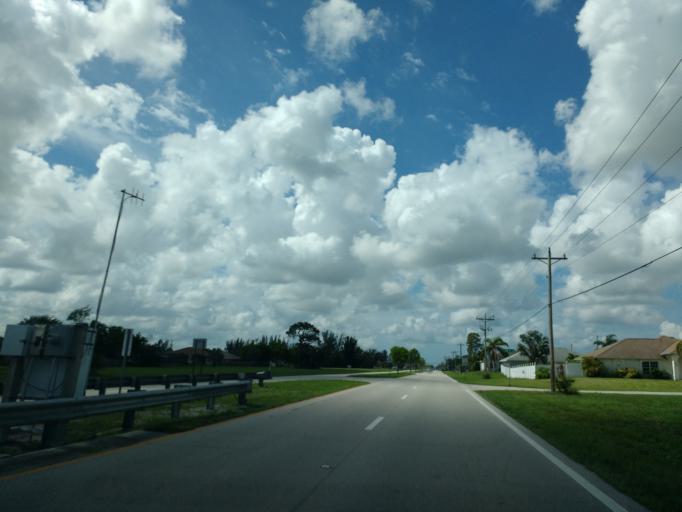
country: US
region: Florida
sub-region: Lee County
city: Cape Coral
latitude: 26.6277
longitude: -82.0073
